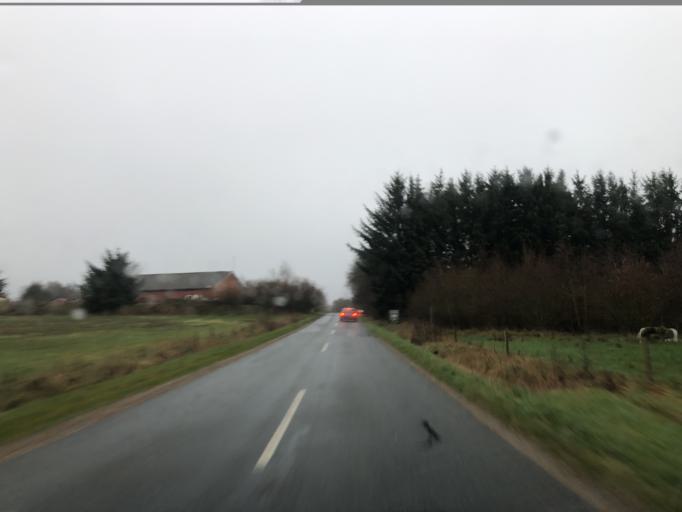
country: DK
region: Central Jutland
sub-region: Holstebro Kommune
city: Ulfborg
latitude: 56.2015
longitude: 8.4117
